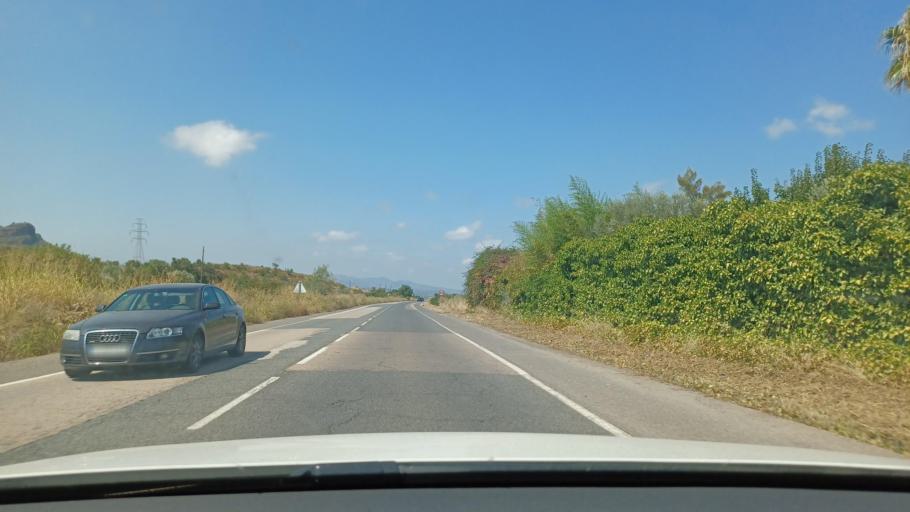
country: ES
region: Valencia
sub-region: Provincia de Valencia
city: Sagunto
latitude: 39.6885
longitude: -0.2631
